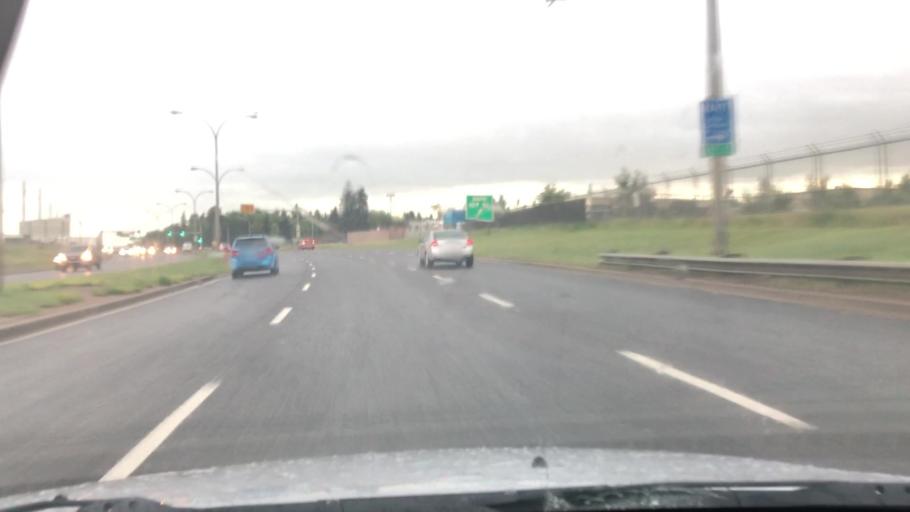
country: CA
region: Alberta
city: Edmonton
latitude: 53.5815
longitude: -113.5096
